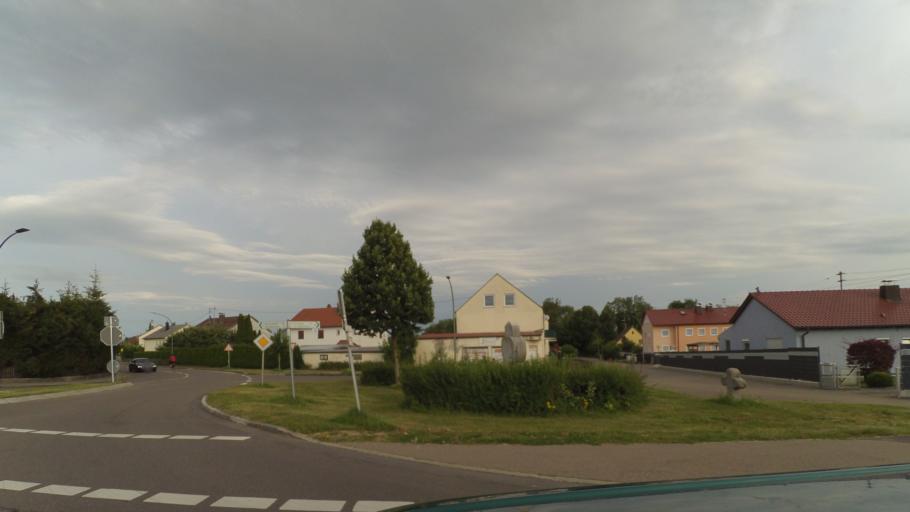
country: DE
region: Bavaria
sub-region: Swabia
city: Hochstadt an der Donau
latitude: 48.6213
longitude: 10.5732
